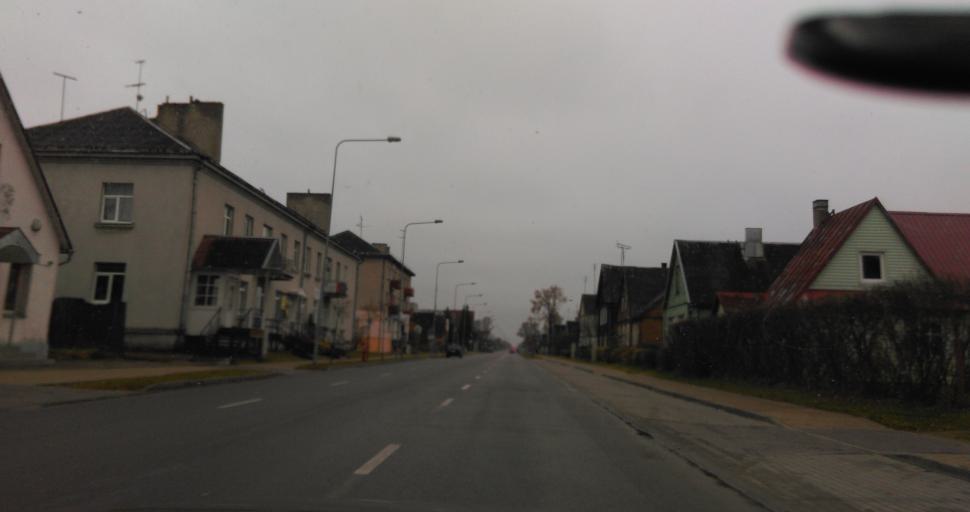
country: LT
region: Panevezys
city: Rokiskis
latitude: 55.9621
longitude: 25.5868
